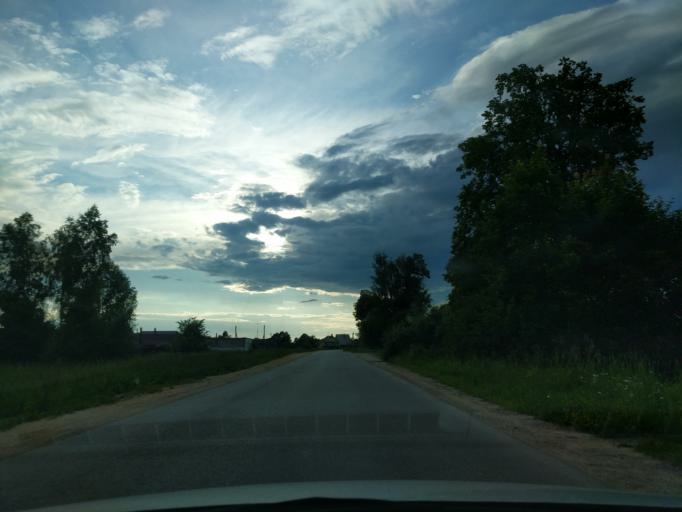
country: RU
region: Kaluga
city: Myatlevo
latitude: 54.8315
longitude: 35.6449
